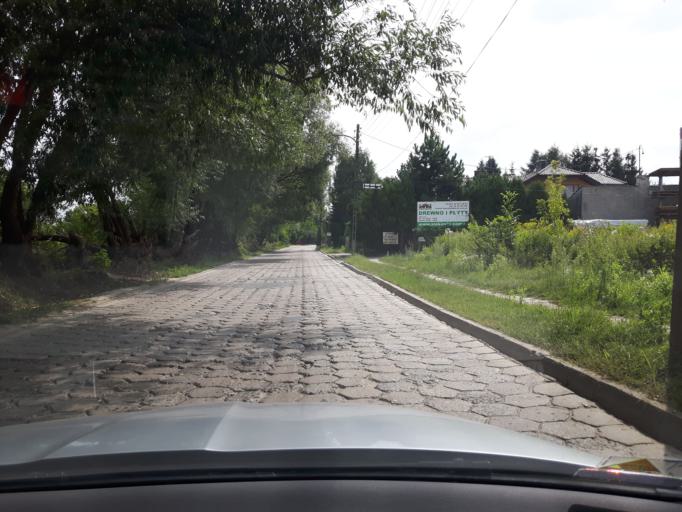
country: PL
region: Masovian Voivodeship
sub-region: Warszawa
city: Wilanow
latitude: 52.1985
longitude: 21.0820
